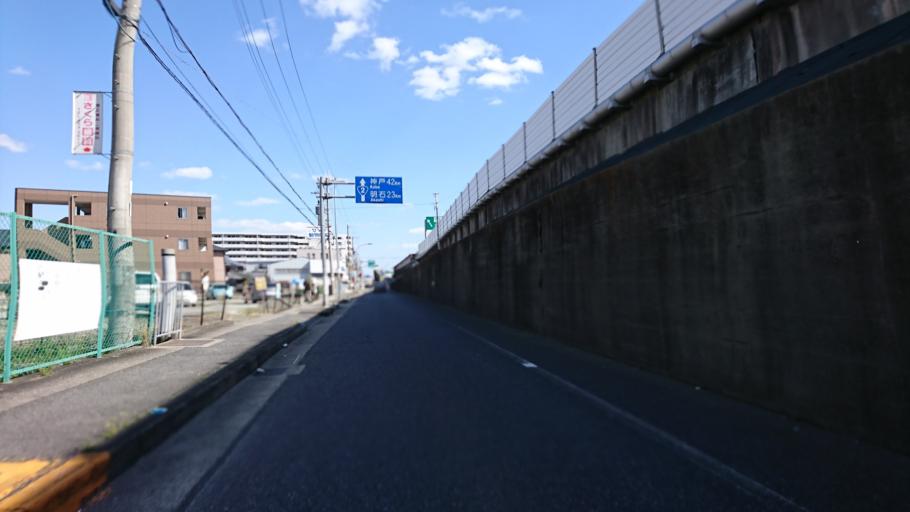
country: JP
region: Hyogo
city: Kakogawacho-honmachi
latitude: 34.7716
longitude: 134.8441
